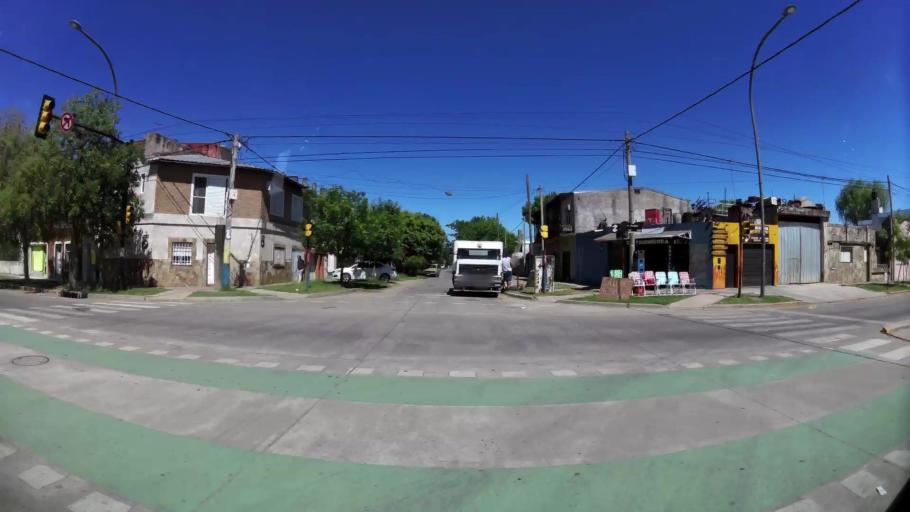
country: AR
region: Santa Fe
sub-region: Departamento de Rosario
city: Rosario
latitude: -32.9659
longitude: -60.7014
